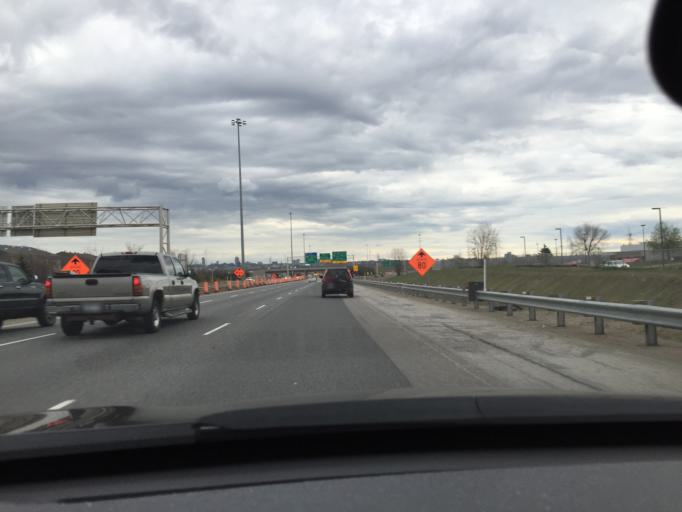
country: CA
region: Quebec
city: Quebec
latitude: 46.8423
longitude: -71.2693
